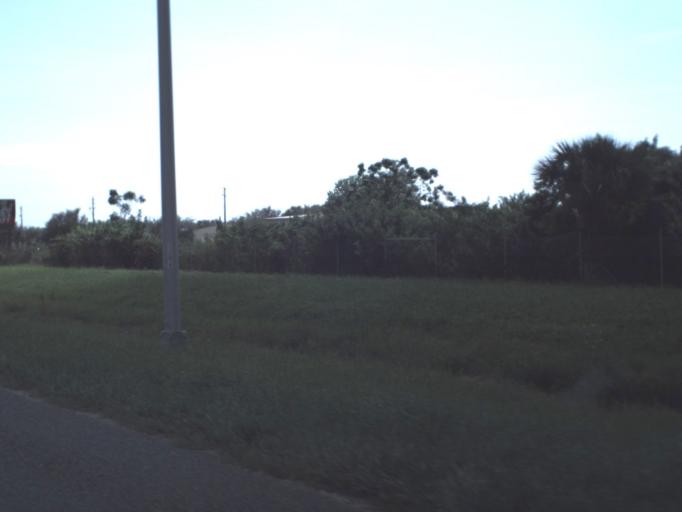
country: US
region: Florida
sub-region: Manatee County
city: Whitfield
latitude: 27.4156
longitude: -82.5330
